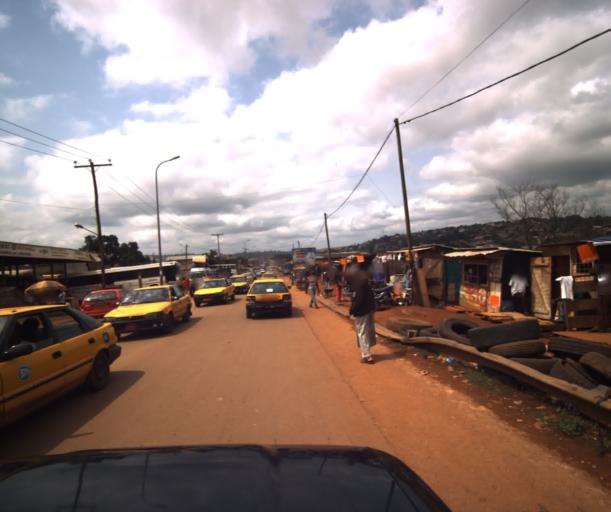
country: CM
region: Centre
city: Yaounde
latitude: 3.8194
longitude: 11.5143
